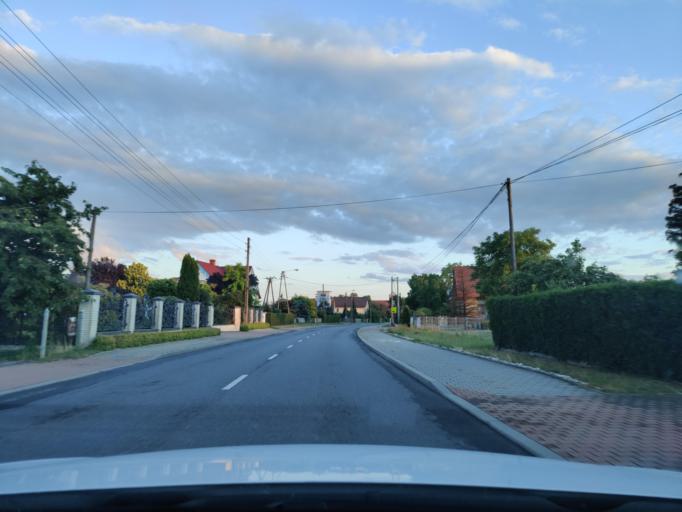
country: PL
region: Opole Voivodeship
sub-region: Powiat brzeski
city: Grodkow
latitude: 50.6595
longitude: 17.3893
